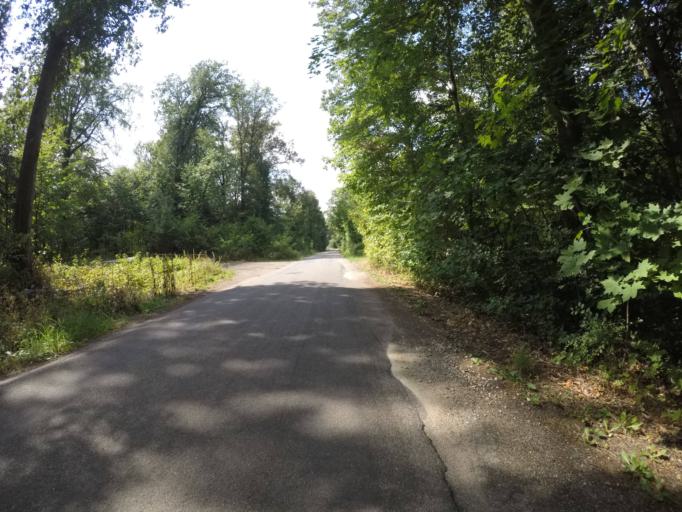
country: DE
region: North Rhine-Westphalia
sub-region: Regierungsbezirk Munster
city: Isselburg
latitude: 51.8324
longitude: 6.4351
